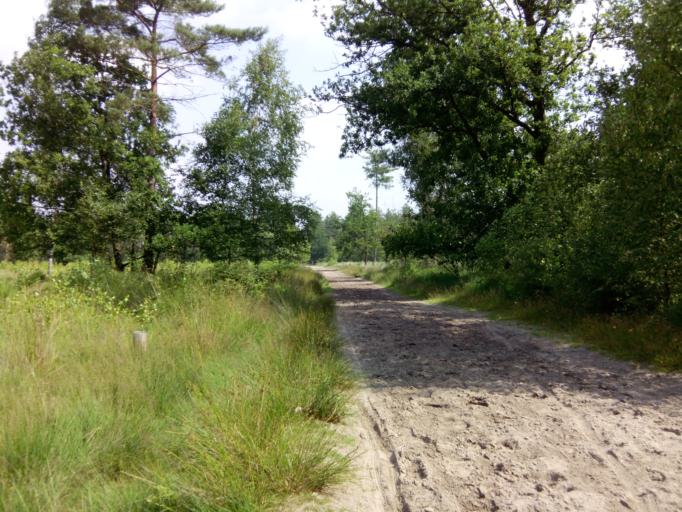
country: NL
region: Utrecht
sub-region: Gemeente Utrechtse Heuvelrug
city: Maarn
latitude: 52.0935
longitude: 5.3789
